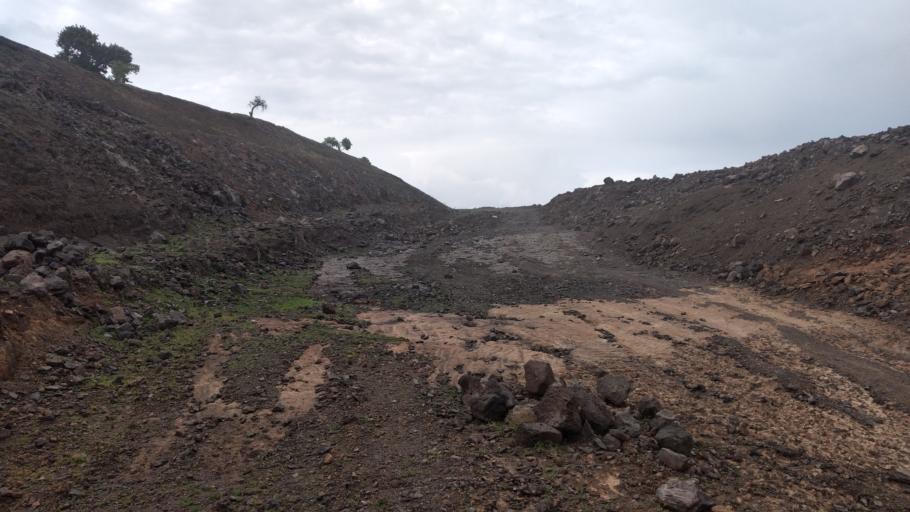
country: ET
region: Southern Nations, Nationalities, and People's Region
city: Areka
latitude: 7.4789
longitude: 37.5033
